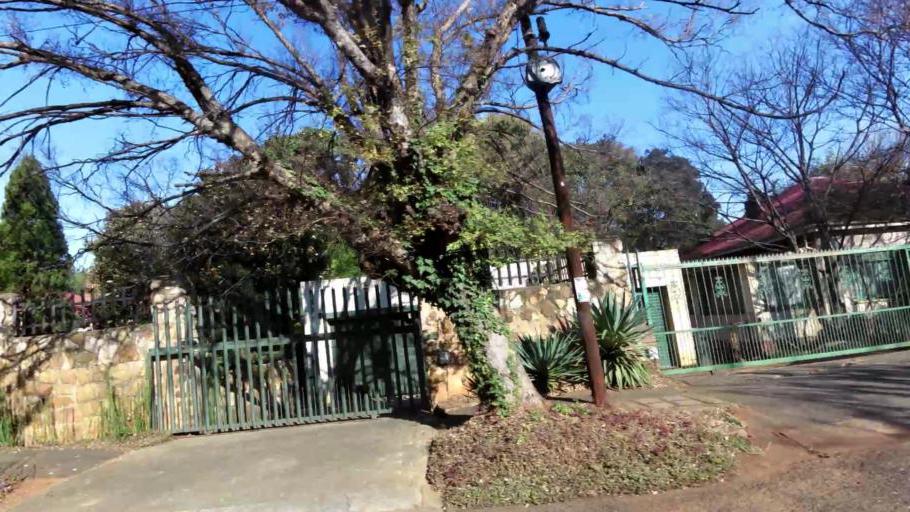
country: ZA
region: Gauteng
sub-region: City of Johannesburg Metropolitan Municipality
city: Johannesburg
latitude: -26.1804
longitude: 28.0085
